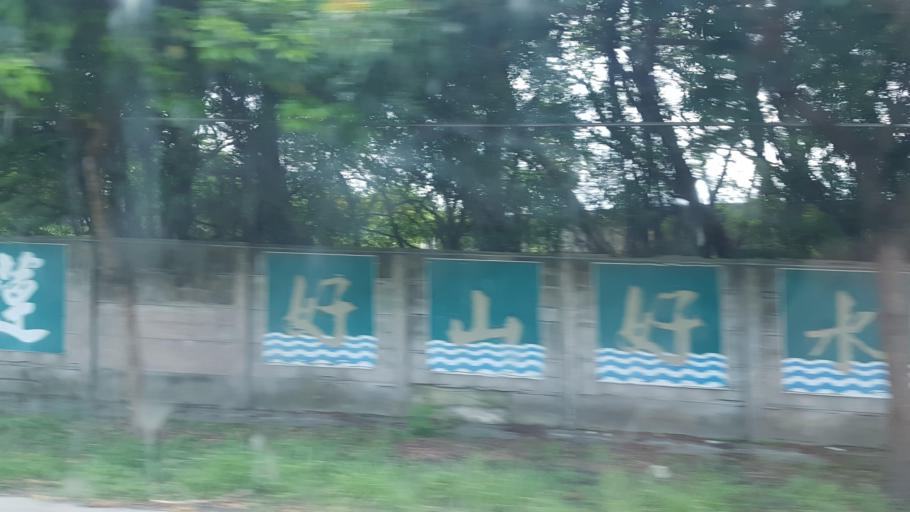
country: TW
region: Taiwan
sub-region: Hualien
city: Hualian
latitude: 23.9251
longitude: 121.5905
